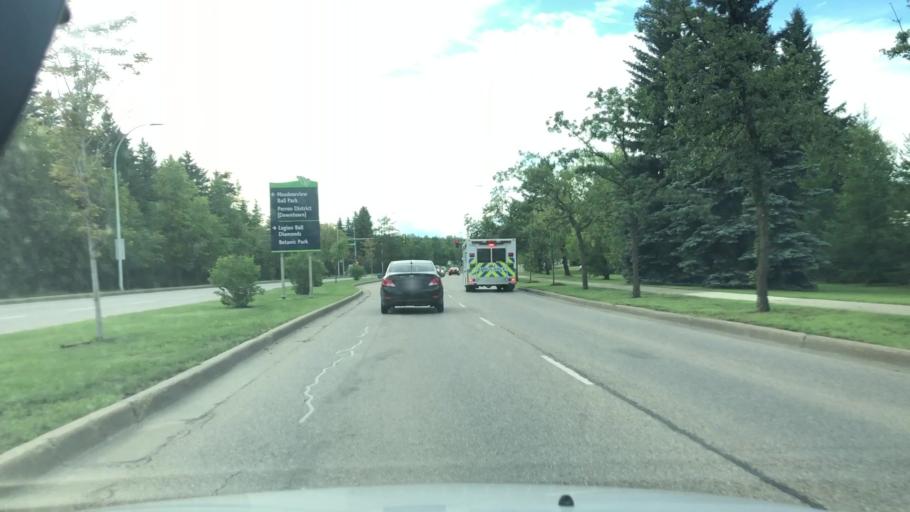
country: CA
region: Alberta
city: St. Albert
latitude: 53.6445
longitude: -113.6090
